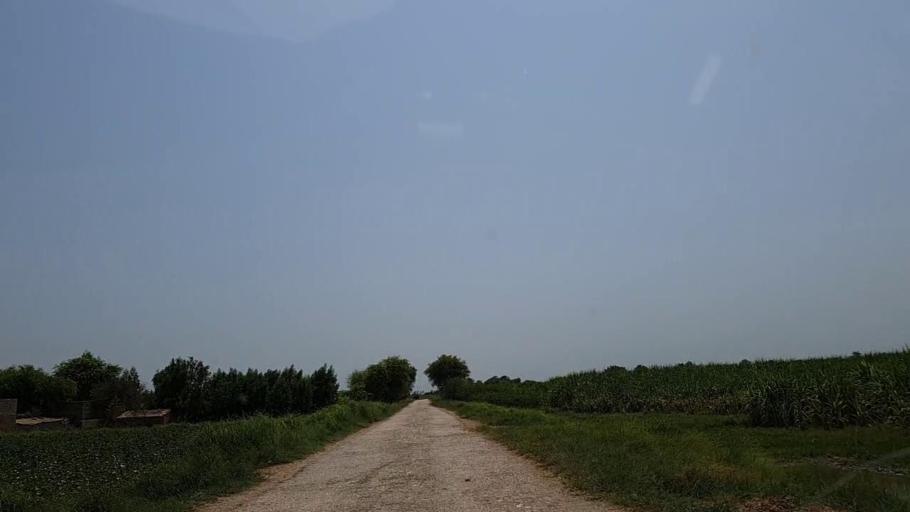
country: PK
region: Sindh
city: Ghotki
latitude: 27.9783
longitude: 69.4022
